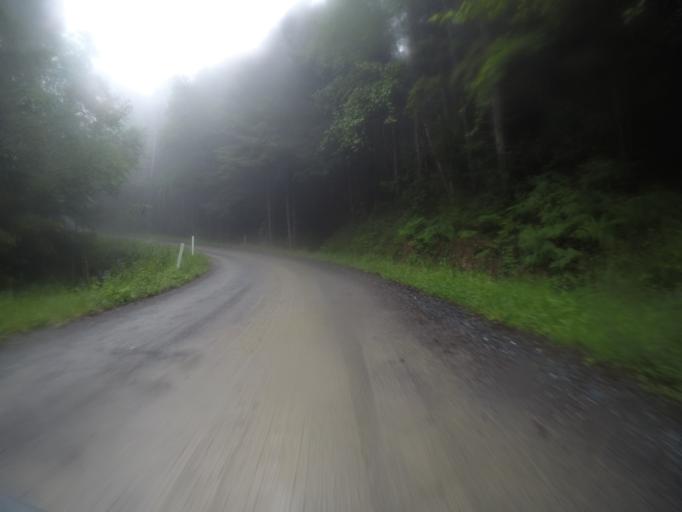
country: US
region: California
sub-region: Humboldt County
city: Westhaven-Moonstone
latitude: 41.2434
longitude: -123.9877
